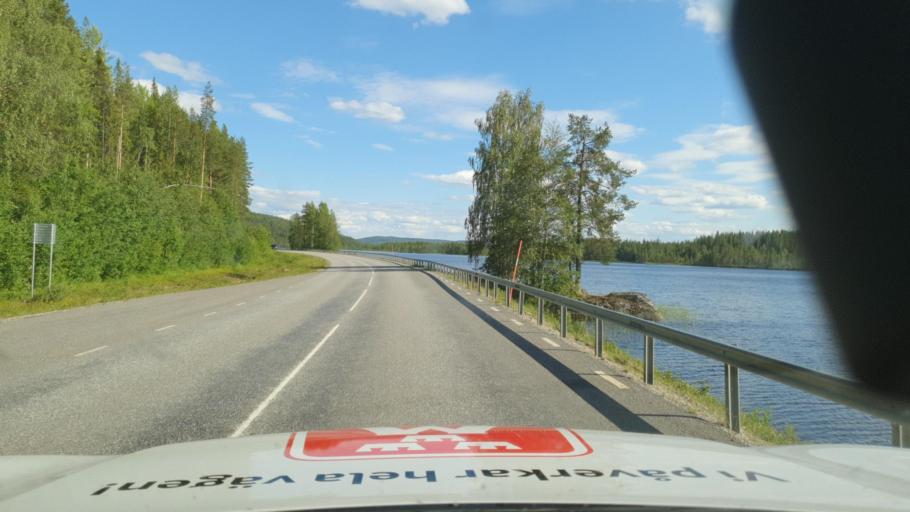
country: SE
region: Vaesterbotten
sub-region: Norsjo Kommun
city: Norsjoe
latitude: 64.8593
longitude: 19.7307
